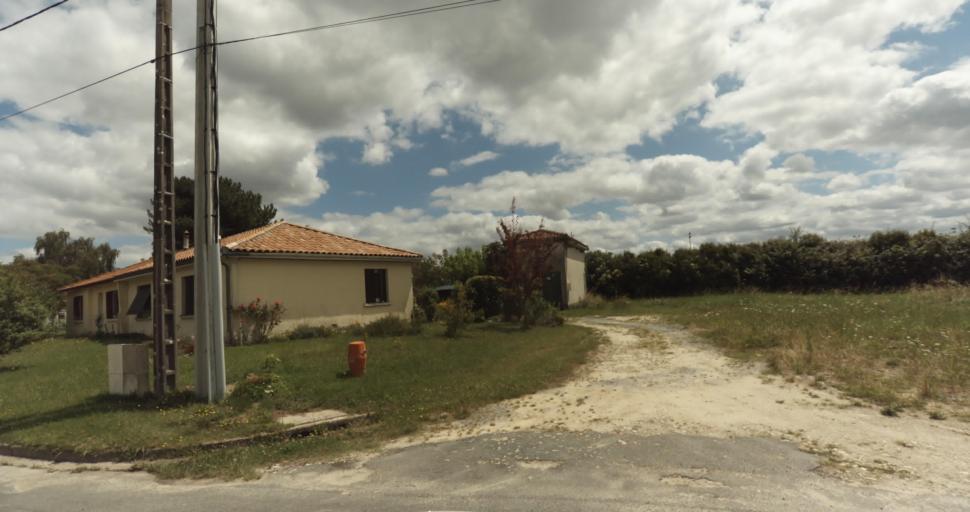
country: FR
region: Aquitaine
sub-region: Departement de la Gironde
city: Bazas
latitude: 44.4355
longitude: -0.2238
